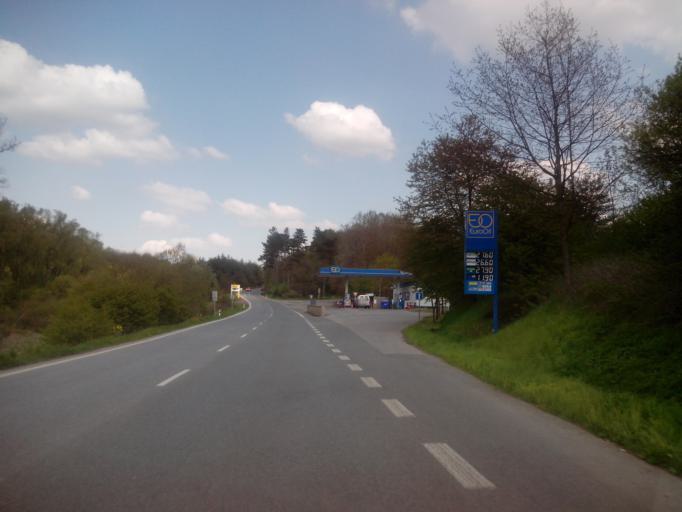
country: CZ
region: Central Bohemia
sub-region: Okres Beroun
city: Beroun
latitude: 49.9746
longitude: 14.0994
